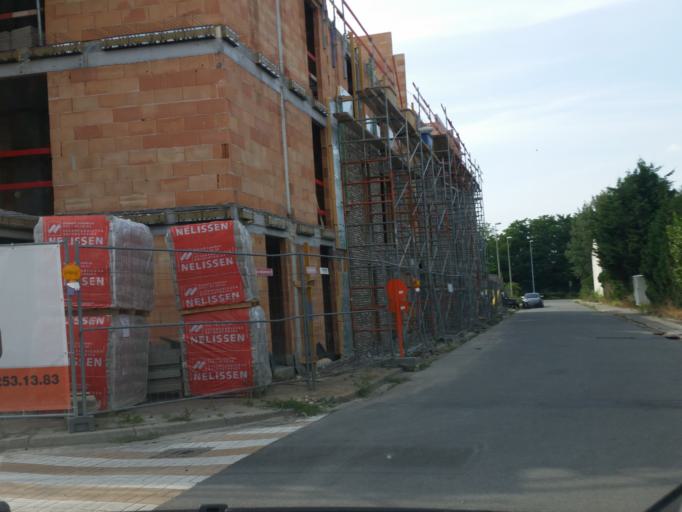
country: BE
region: Flanders
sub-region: Provincie Vlaams-Brabant
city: Vilvoorde
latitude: 50.9347
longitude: 4.4200
